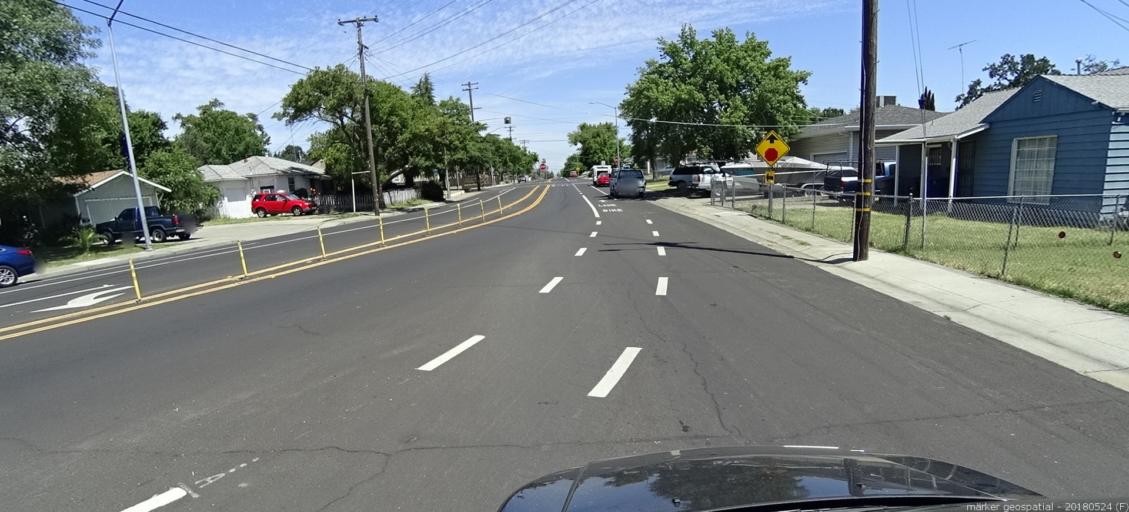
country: US
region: California
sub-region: Sacramento County
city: Sacramento
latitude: 38.6143
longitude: -121.4570
